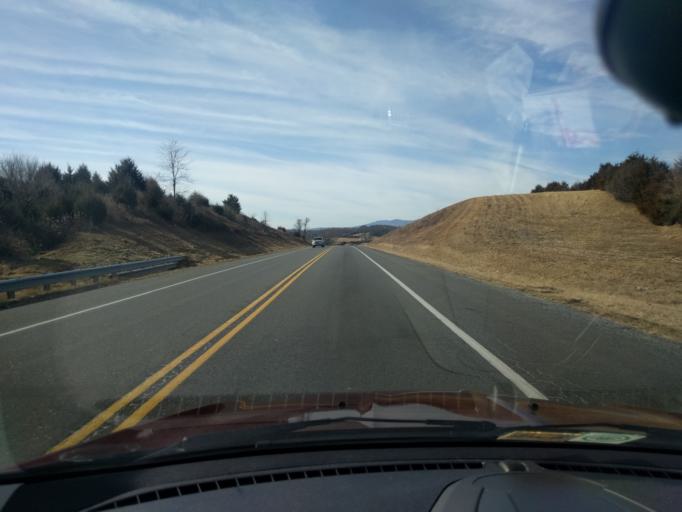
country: US
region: Virginia
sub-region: Augusta County
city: Verona
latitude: 38.1879
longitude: -79.0463
